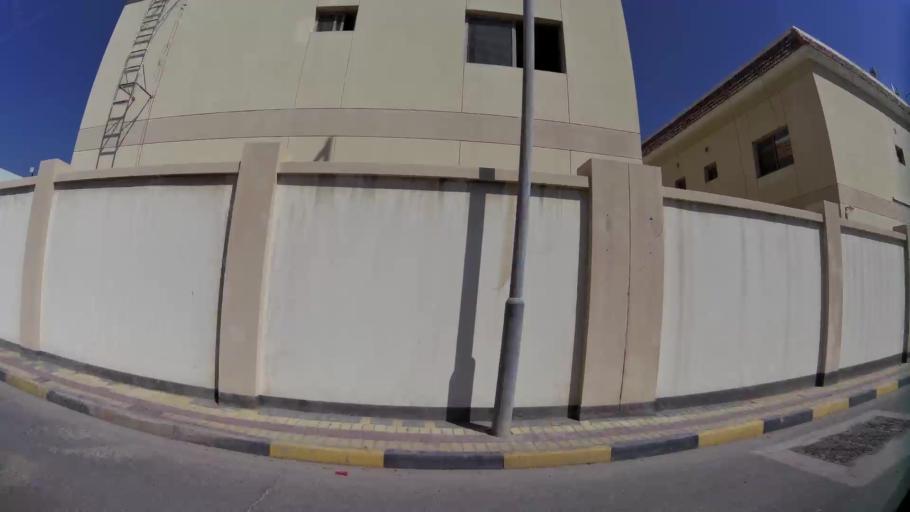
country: BH
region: Manama
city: Manama
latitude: 26.2098
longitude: 50.6051
